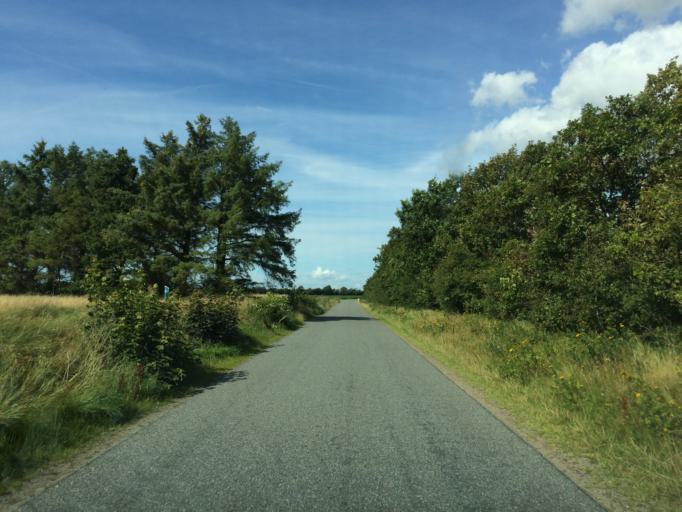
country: DK
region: Central Jutland
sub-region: Ringkobing-Skjern Kommune
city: Skjern
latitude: 55.9683
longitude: 8.3705
